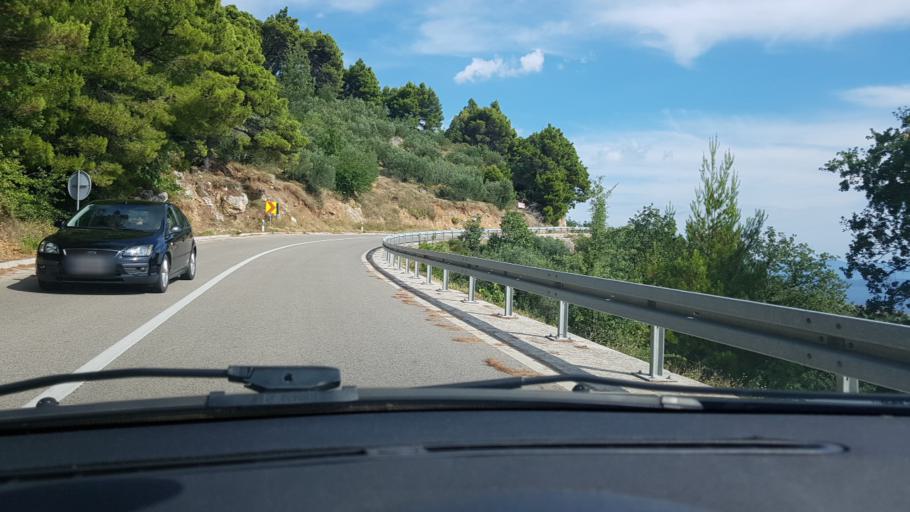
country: HR
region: Splitsko-Dalmatinska
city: Tucepi
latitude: 43.2764
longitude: 17.0636
